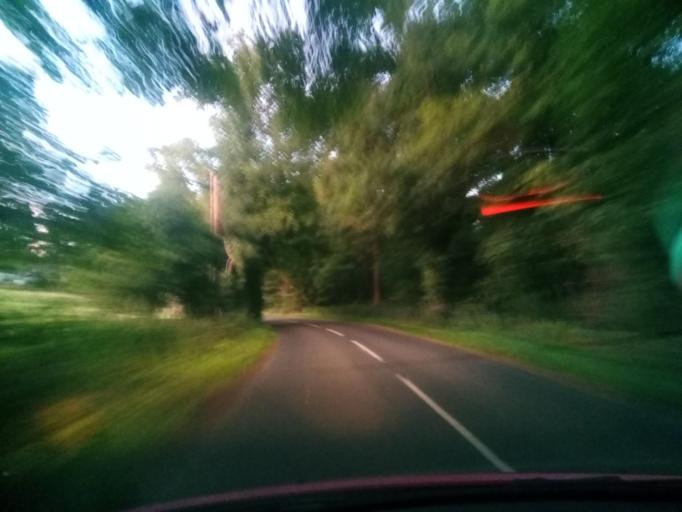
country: GB
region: England
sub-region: Northumberland
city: Wall
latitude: 55.0258
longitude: -2.1491
